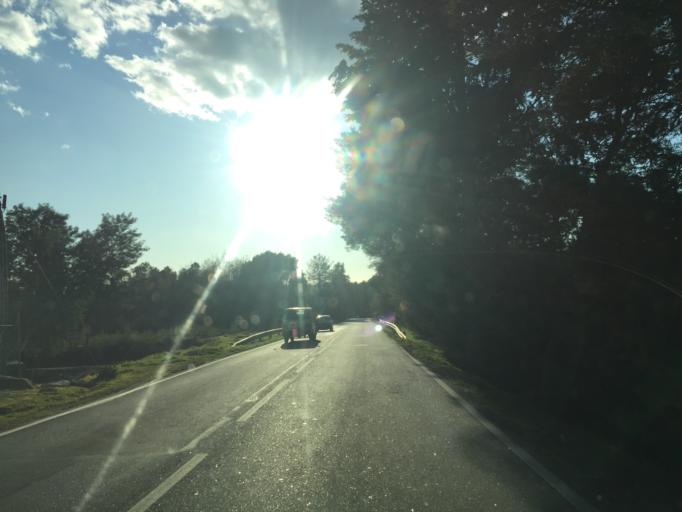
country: PT
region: Viseu
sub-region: Nelas
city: Nelas
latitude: 40.5172
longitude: -7.8779
